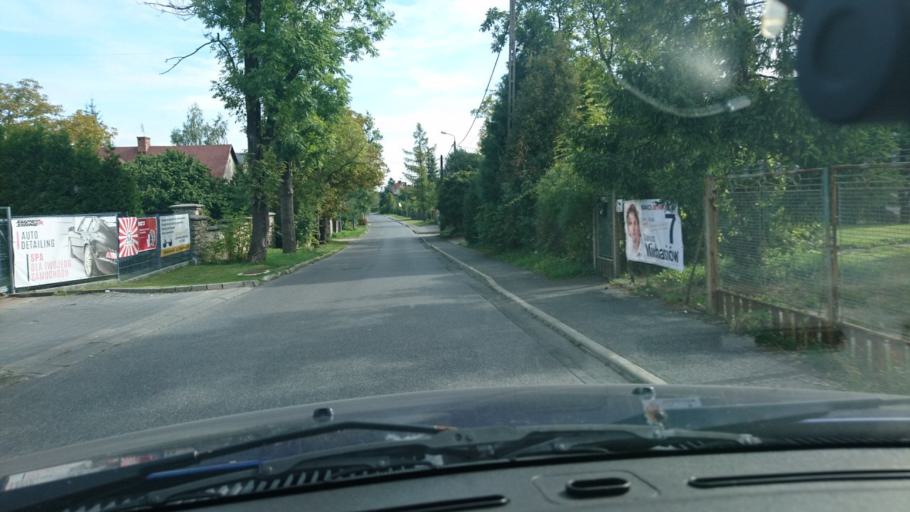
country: PL
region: Silesian Voivodeship
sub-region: Powiat bielski
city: Mazancowice
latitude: 49.8218
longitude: 19.0020
